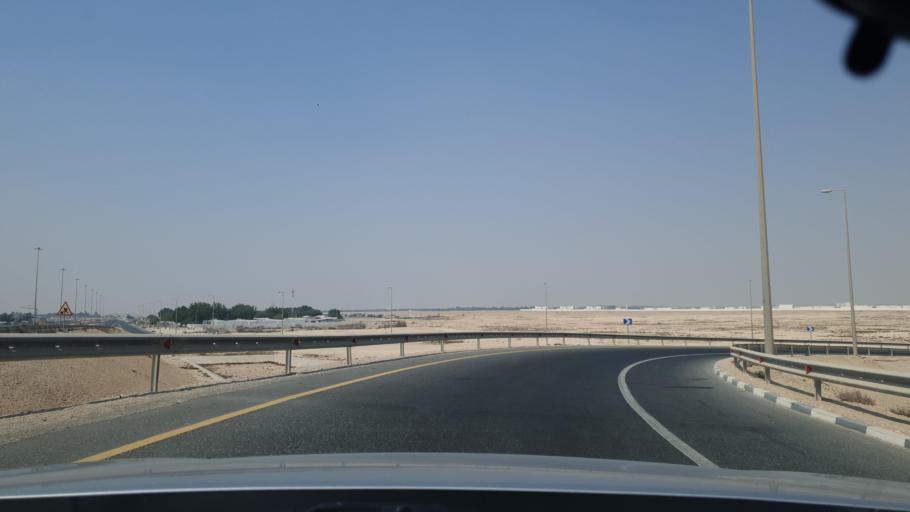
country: QA
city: Al Ghuwayriyah
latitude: 25.8299
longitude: 51.3481
